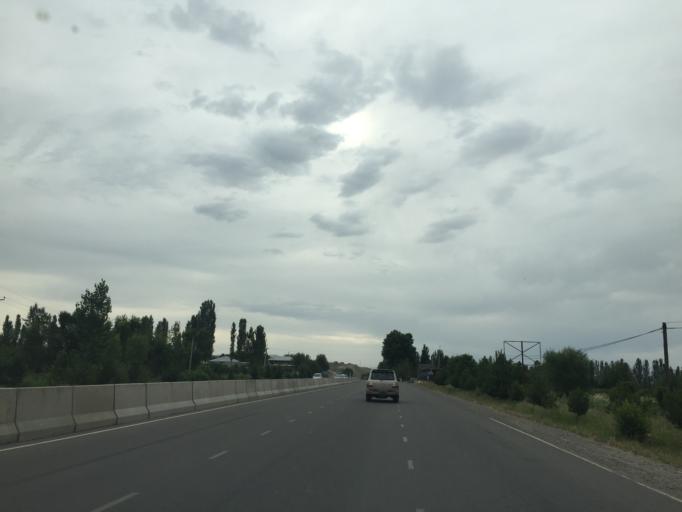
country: TJ
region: Republican Subordination
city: Vahdat
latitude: 38.5558
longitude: 68.9445
